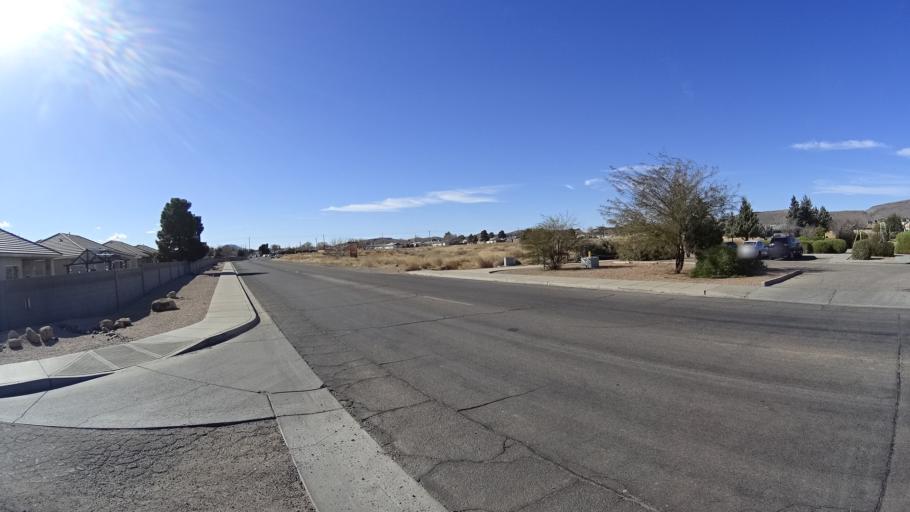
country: US
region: Arizona
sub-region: Mohave County
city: New Kingman-Butler
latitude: 35.2345
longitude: -114.0248
